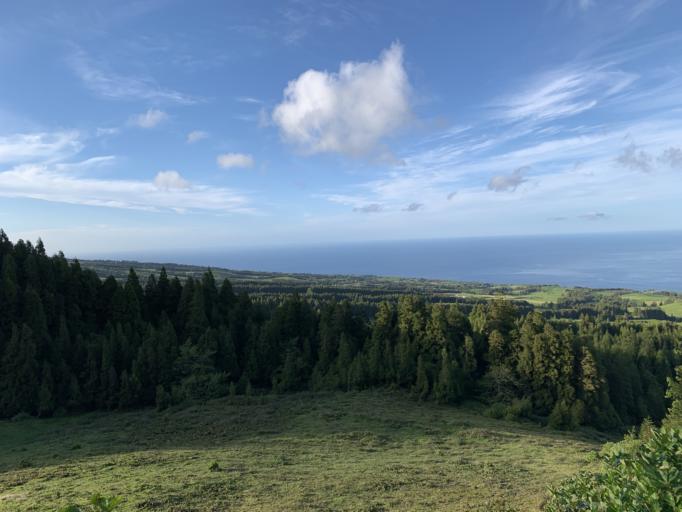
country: PT
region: Azores
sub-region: Ponta Delgada
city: Arrifes
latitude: 37.8254
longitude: -25.7389
